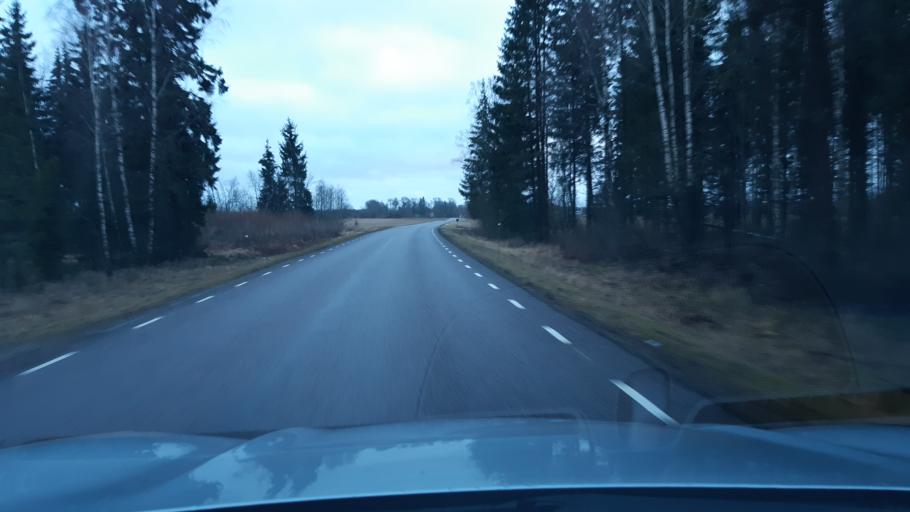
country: EE
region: Raplamaa
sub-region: Kohila vald
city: Kohila
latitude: 59.1226
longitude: 24.6761
